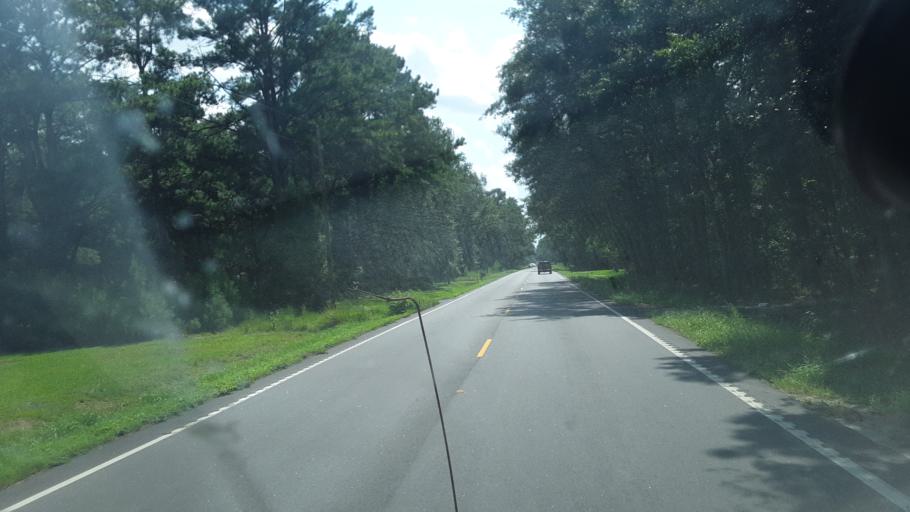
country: US
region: Georgia
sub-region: Chatham County
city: Savannah
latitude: 32.1713
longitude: -81.0334
